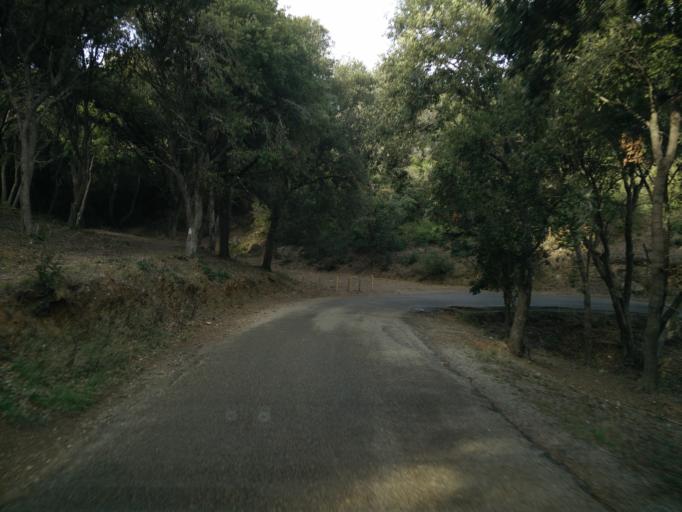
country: FR
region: Provence-Alpes-Cote d'Azur
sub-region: Departement du Var
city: Six-Fours-les-Plages
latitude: 43.0565
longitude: 5.8361
